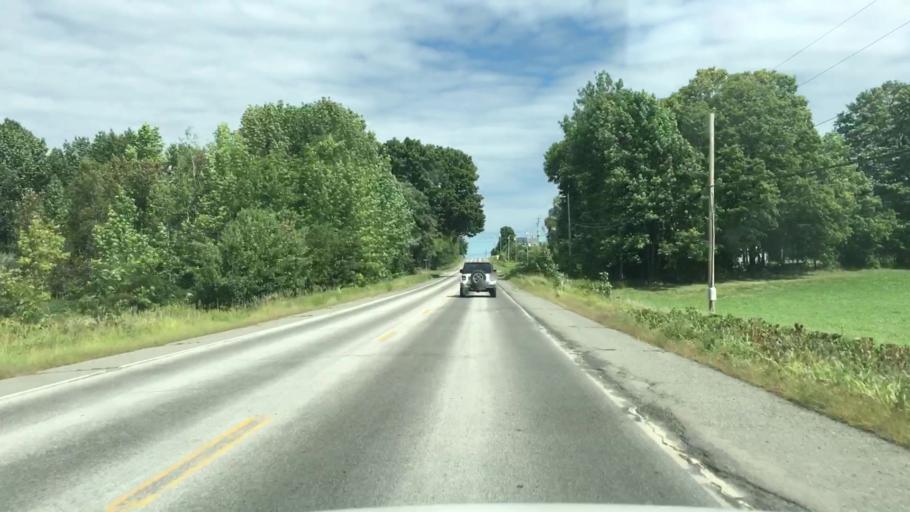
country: US
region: Maine
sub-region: Piscataquis County
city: Dover-Foxcroft
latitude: 45.1592
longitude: -69.2329
